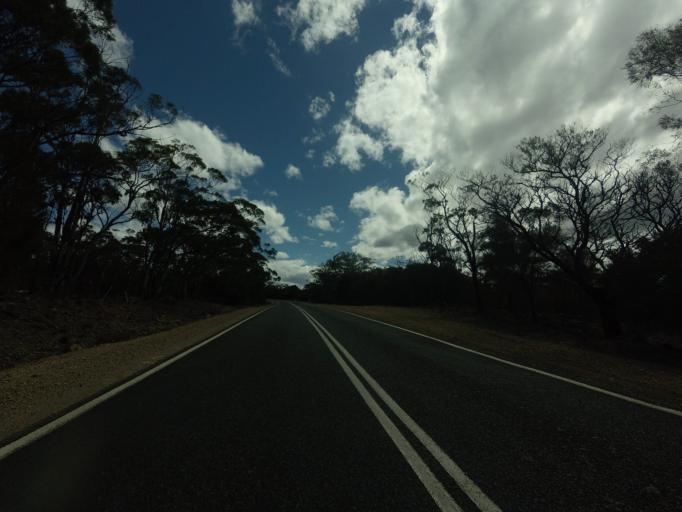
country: AU
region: Tasmania
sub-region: Break O'Day
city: St Helens
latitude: -42.0125
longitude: 147.9911
